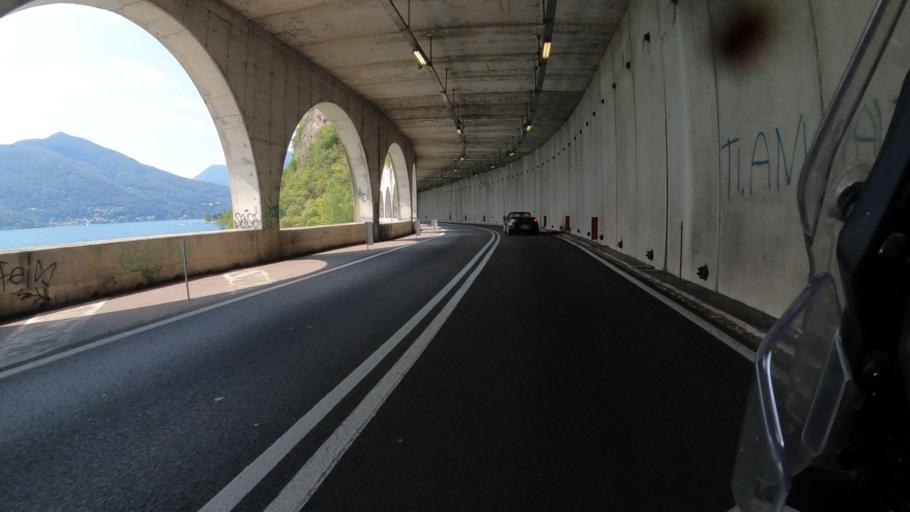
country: IT
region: Lombardy
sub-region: Provincia di Varese
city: Maccagno
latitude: 46.0326
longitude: 8.7471
